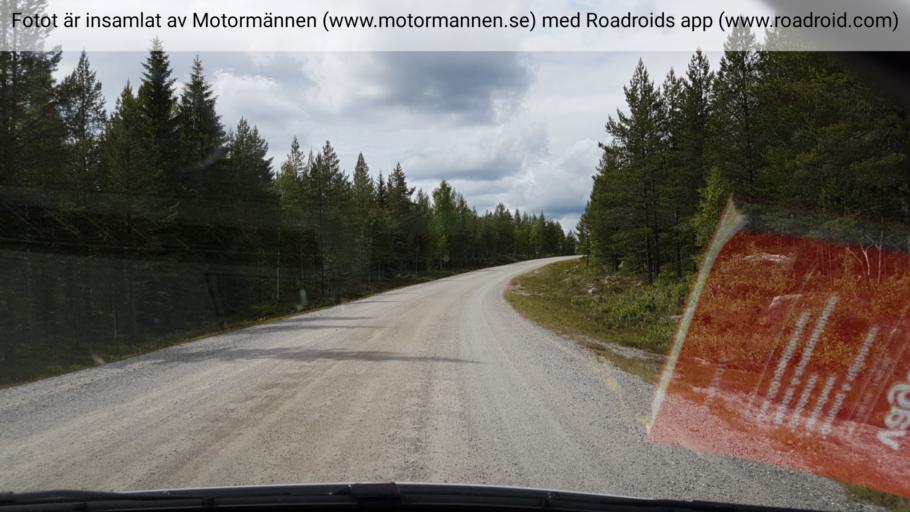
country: SE
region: Vaesternorrland
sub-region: Solleftea Kommun
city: Solleftea
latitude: 63.3225
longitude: 17.3739
